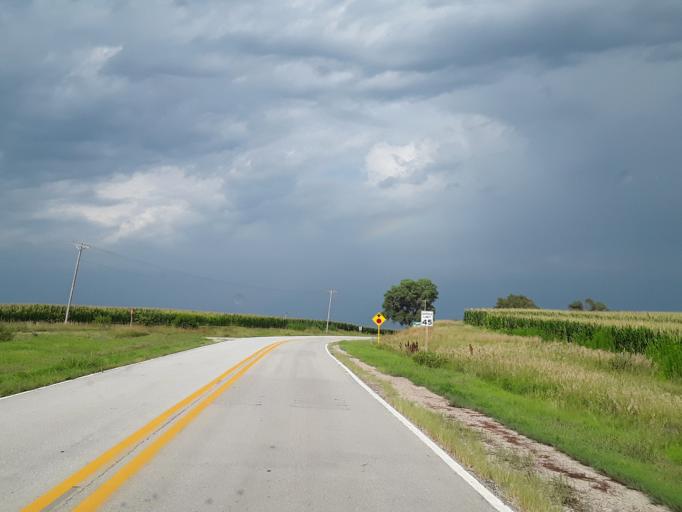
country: US
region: Nebraska
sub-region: Saunders County
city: Ashland
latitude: 41.0955
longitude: -96.4291
